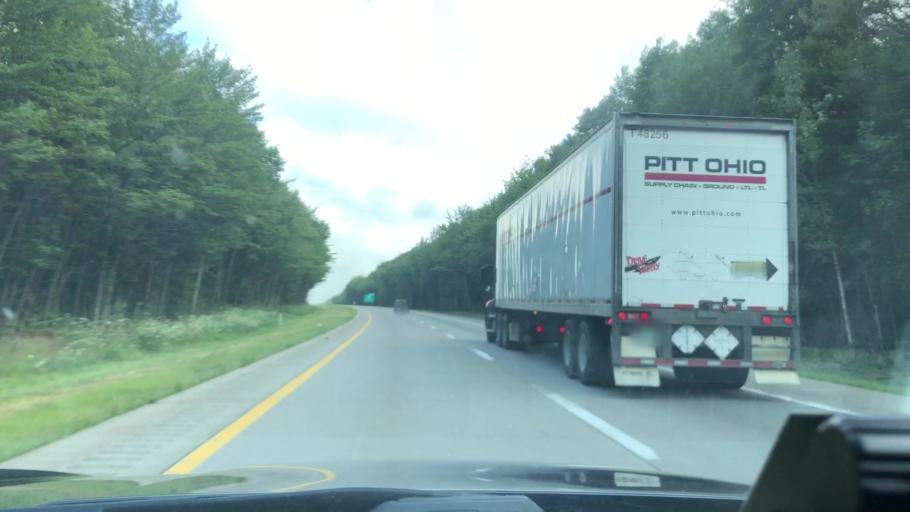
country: US
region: Pennsylvania
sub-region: Monroe County
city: Mount Pocono
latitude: 41.1454
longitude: -75.4039
